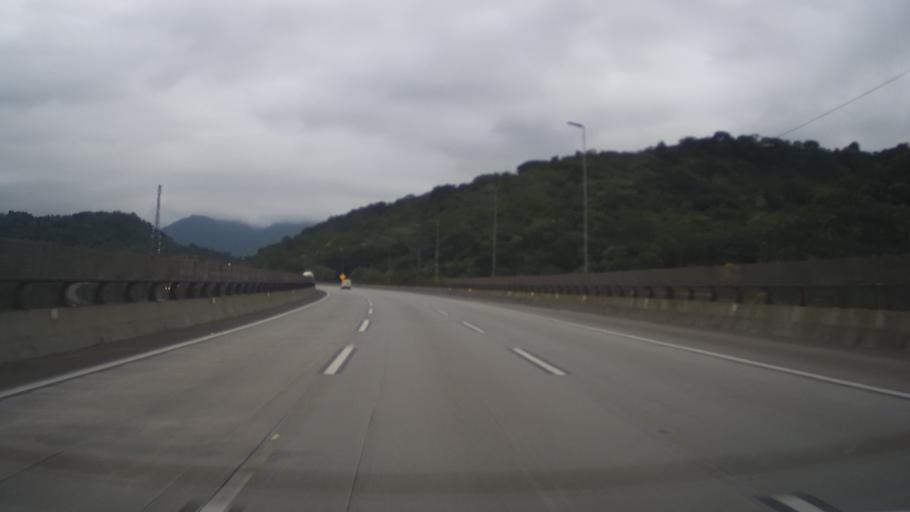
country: BR
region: Sao Paulo
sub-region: Cubatao
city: Cubatao
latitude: -23.9033
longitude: -46.4534
